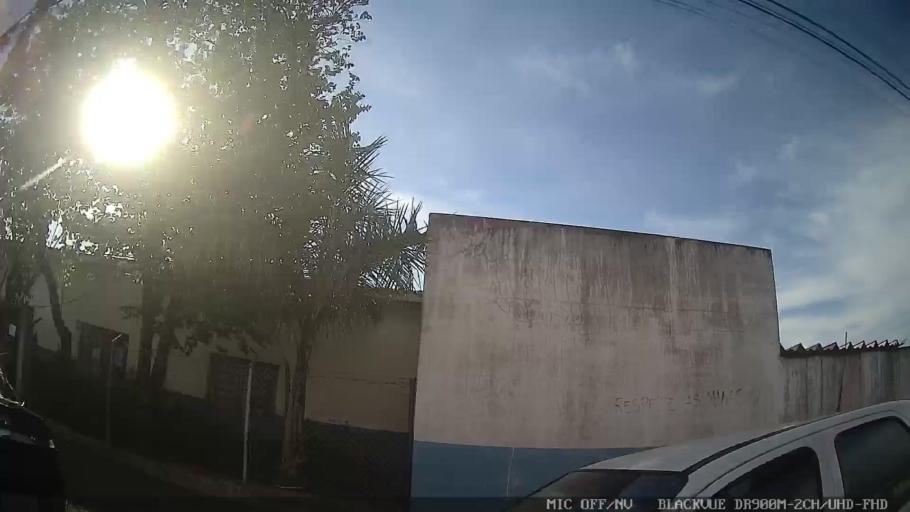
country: BR
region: Sao Paulo
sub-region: Tiete
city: Tiete
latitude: -23.0928
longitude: -47.6995
